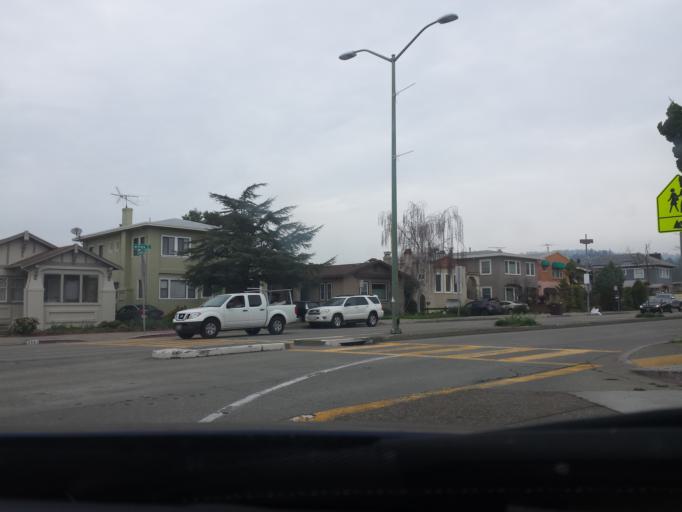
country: US
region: California
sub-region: Alameda County
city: Piedmont
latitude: 37.8051
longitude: -122.2270
